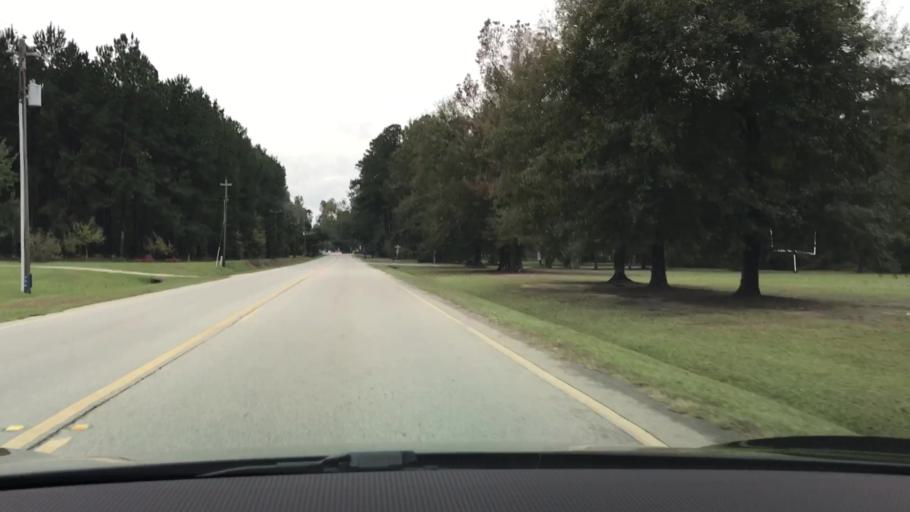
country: US
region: Georgia
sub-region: Jefferson County
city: Wrens
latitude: 33.2199
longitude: -82.4651
